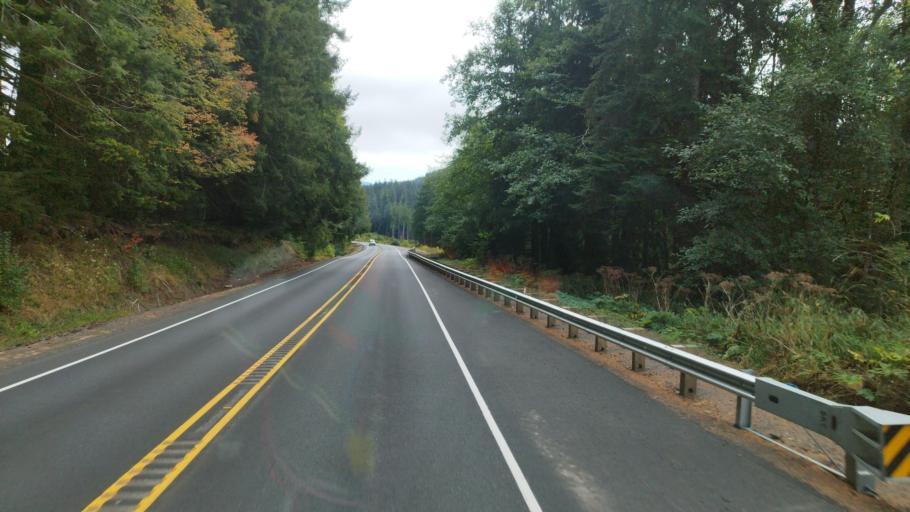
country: US
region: Oregon
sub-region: Clatsop County
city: Seaside
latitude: 45.8975
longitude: -123.6515
